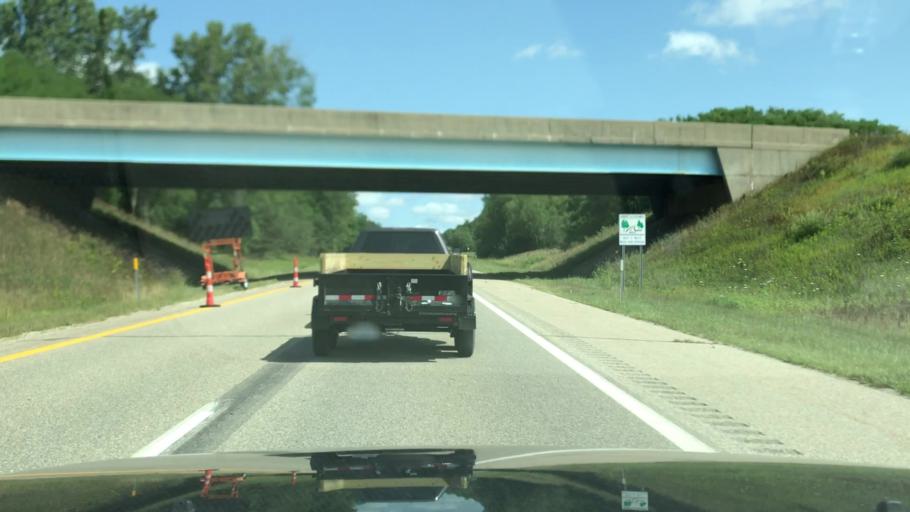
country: US
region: Michigan
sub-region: Mecosta County
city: Big Rapids
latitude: 43.7423
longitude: -85.5306
